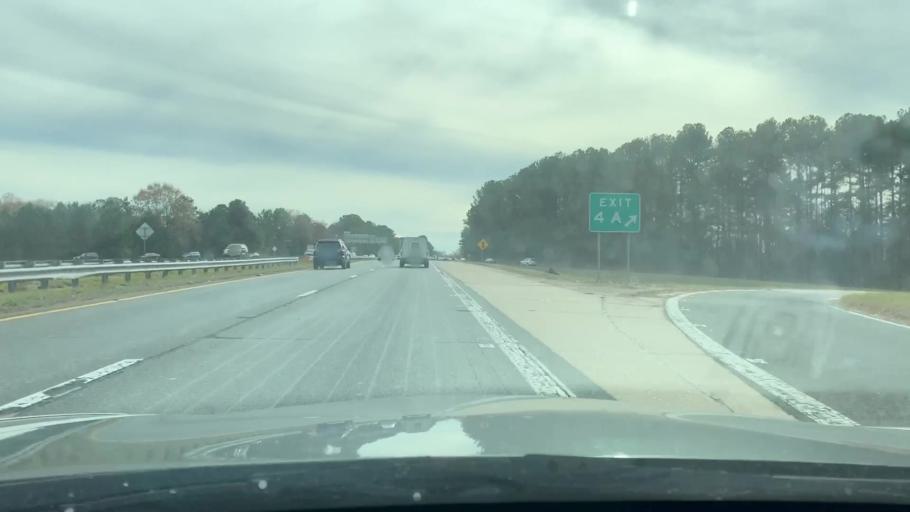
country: US
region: North Carolina
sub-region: Wake County
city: West Raleigh
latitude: 35.8029
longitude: -78.6939
